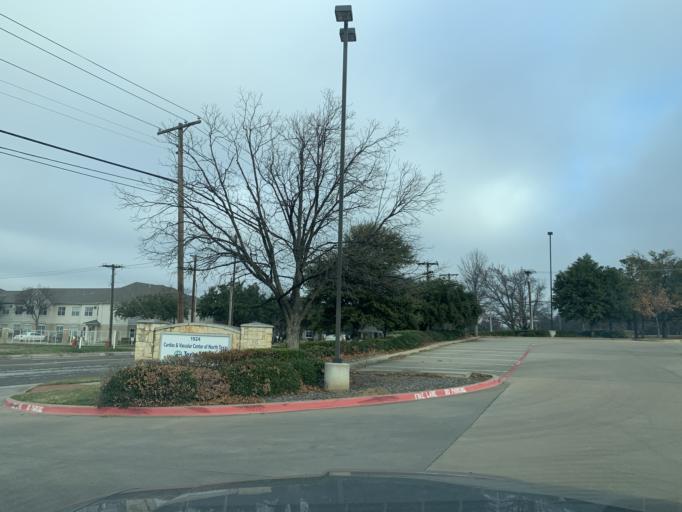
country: US
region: Texas
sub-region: Tarrant County
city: Bedford
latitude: 32.8396
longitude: -97.1416
